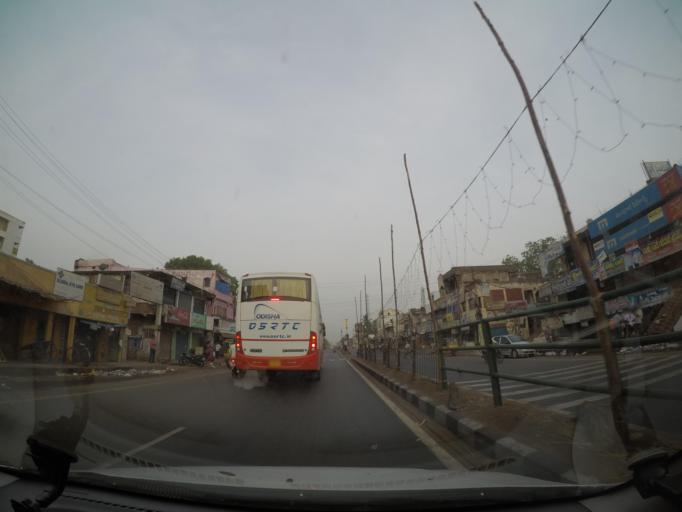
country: IN
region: Andhra Pradesh
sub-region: West Godavari
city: Eluru
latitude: 16.6353
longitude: 80.9704
